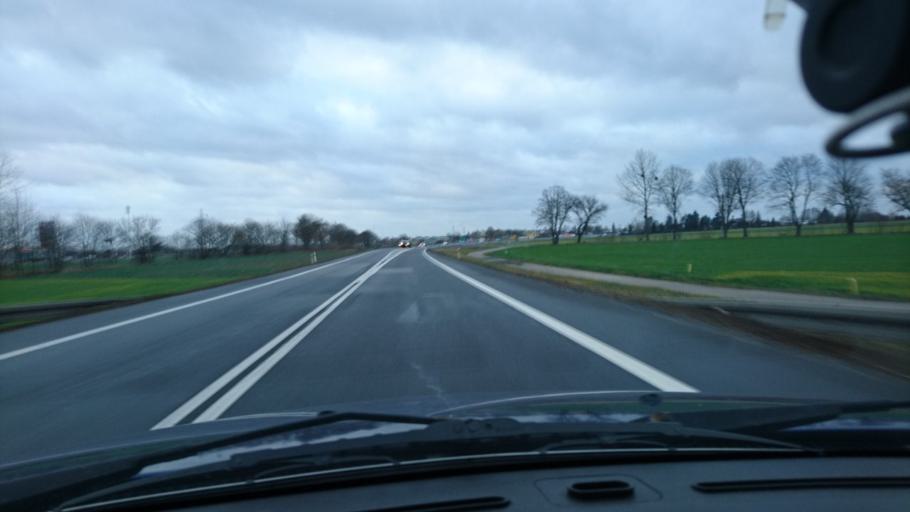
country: PL
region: Opole Voivodeship
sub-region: Powiat kluczborski
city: Kluczbork
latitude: 50.9910
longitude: 18.2180
